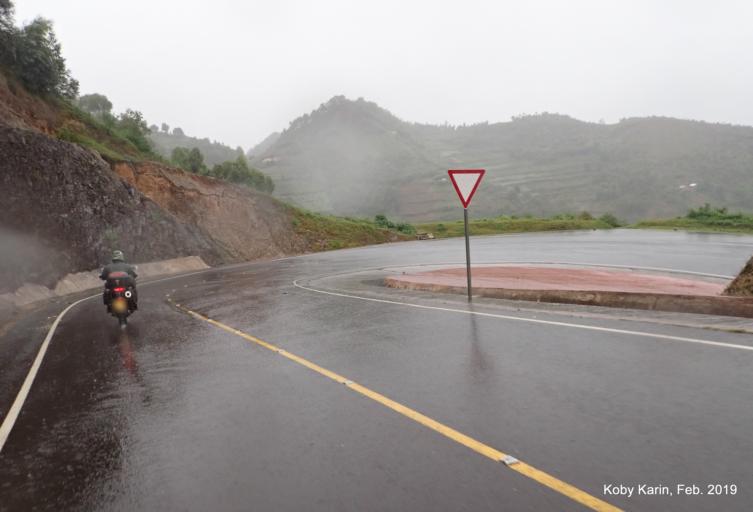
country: UG
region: Western Region
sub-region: Kisoro District
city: Kisoro
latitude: -1.2818
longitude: 29.7660
